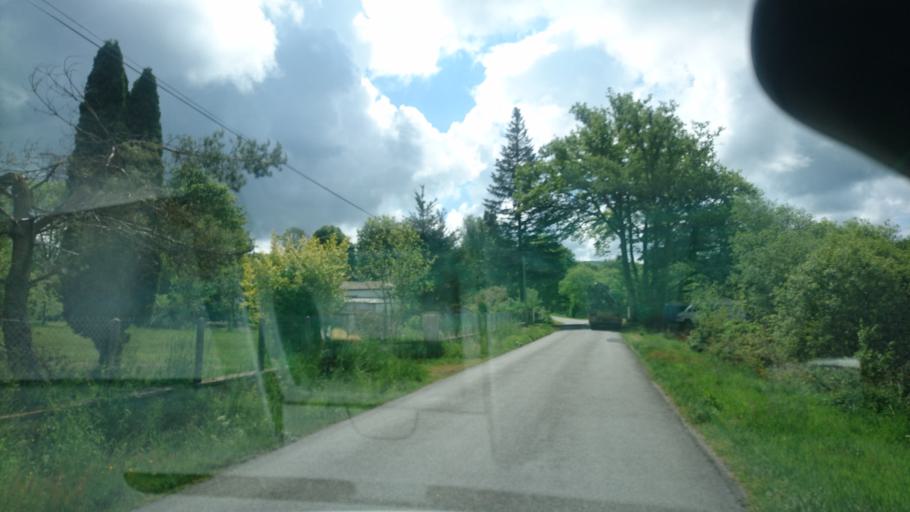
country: FR
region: Limousin
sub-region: Departement de la Haute-Vienne
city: Peyrat-le-Chateau
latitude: 45.7888
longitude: 1.8932
